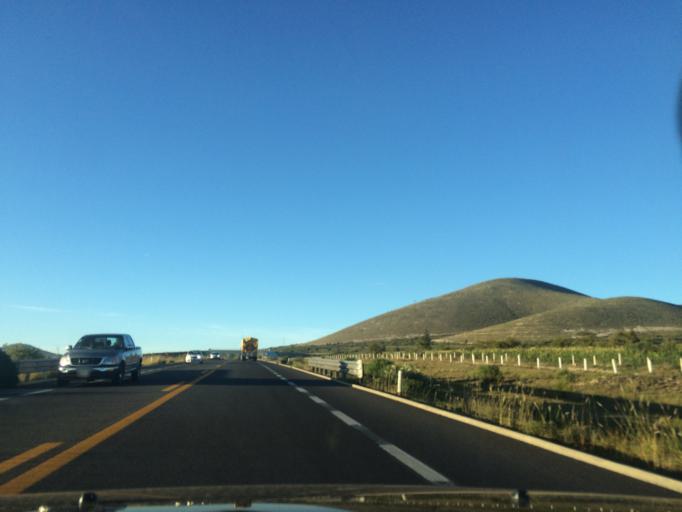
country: MX
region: Puebla
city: Morelos Canada
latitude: 18.7332
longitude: -97.4756
